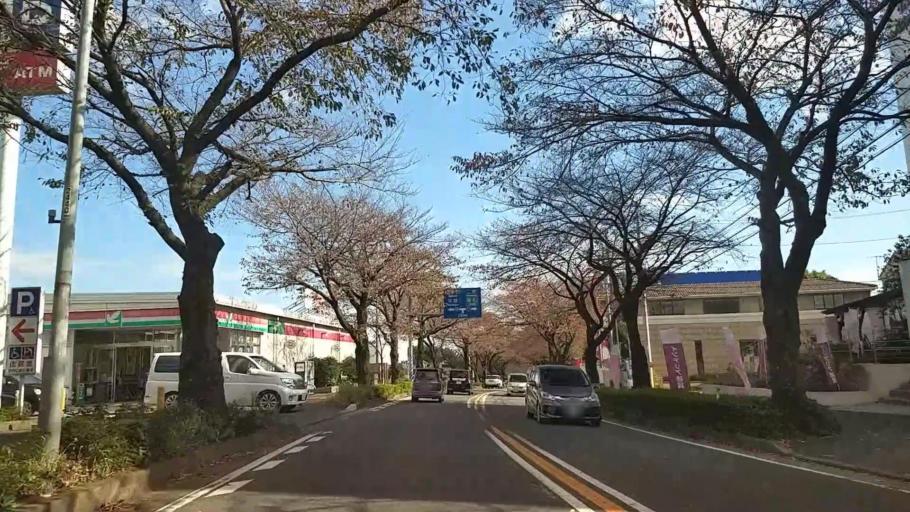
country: JP
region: Kanagawa
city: Hadano
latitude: 35.3619
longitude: 139.2308
